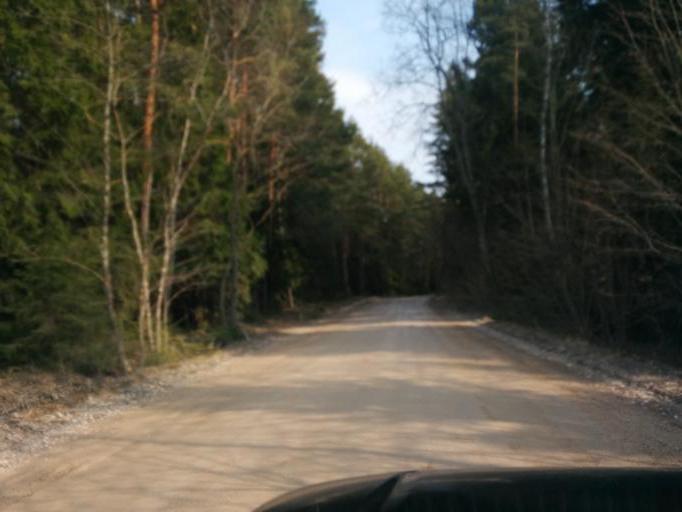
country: LV
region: Olaine
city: Olaine
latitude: 56.7889
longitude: 24.0467
